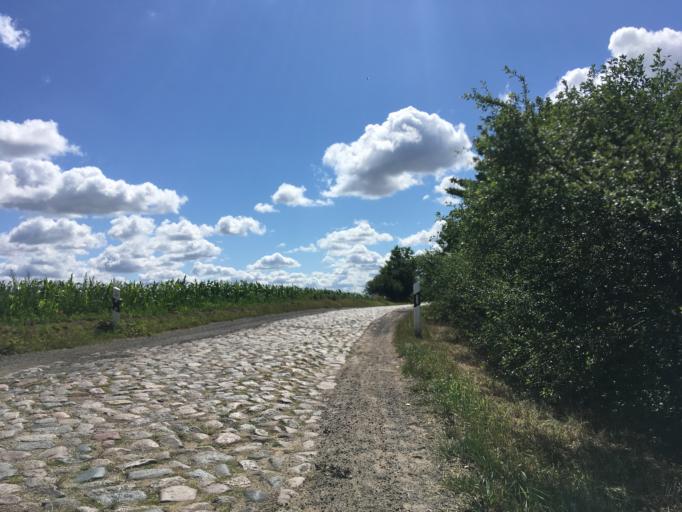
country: DE
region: Brandenburg
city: Mittenwalde
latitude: 53.1911
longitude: 13.6360
